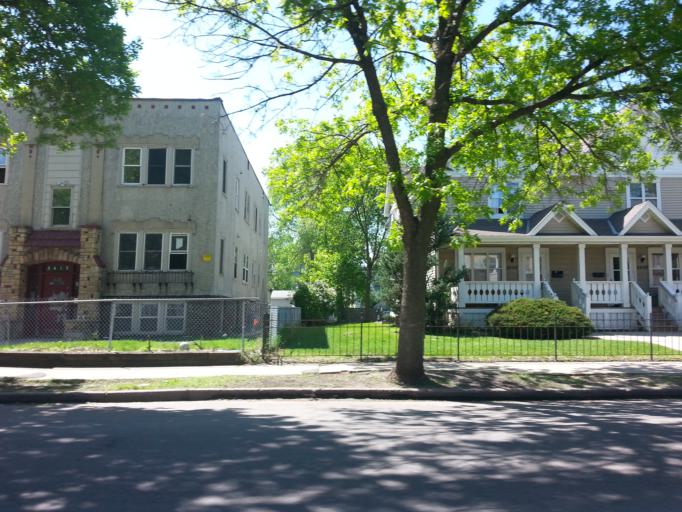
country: US
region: Minnesota
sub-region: Hennepin County
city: Minneapolis
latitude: 44.9408
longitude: -93.2626
